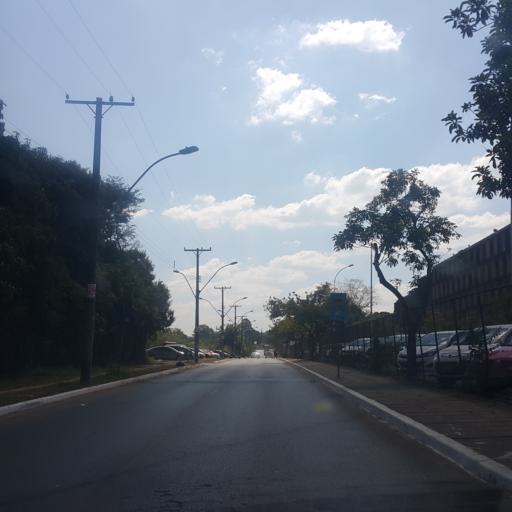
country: BR
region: Federal District
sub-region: Brasilia
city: Brasilia
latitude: -15.8239
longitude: -48.0699
